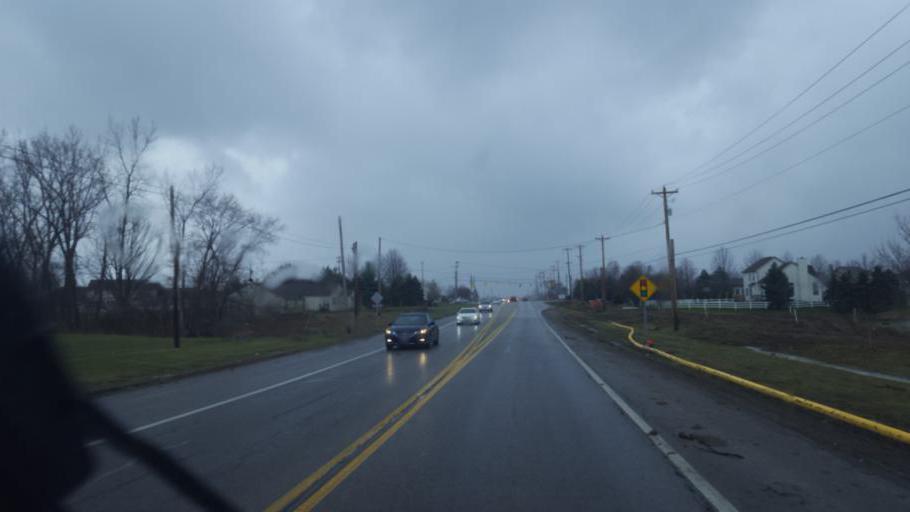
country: US
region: Ohio
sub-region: Delaware County
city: Lewis Center
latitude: 40.1593
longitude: -82.9942
